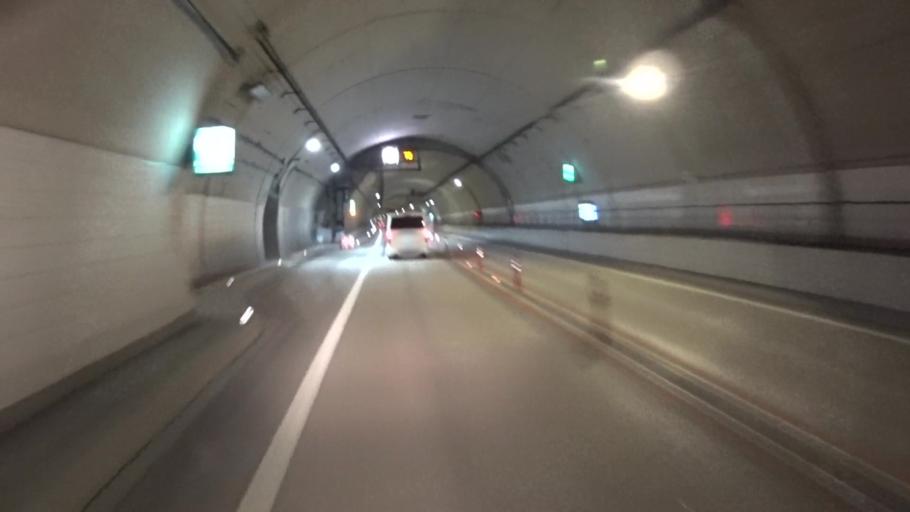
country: JP
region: Kyoto
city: Miyazu
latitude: 35.5230
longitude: 135.1793
